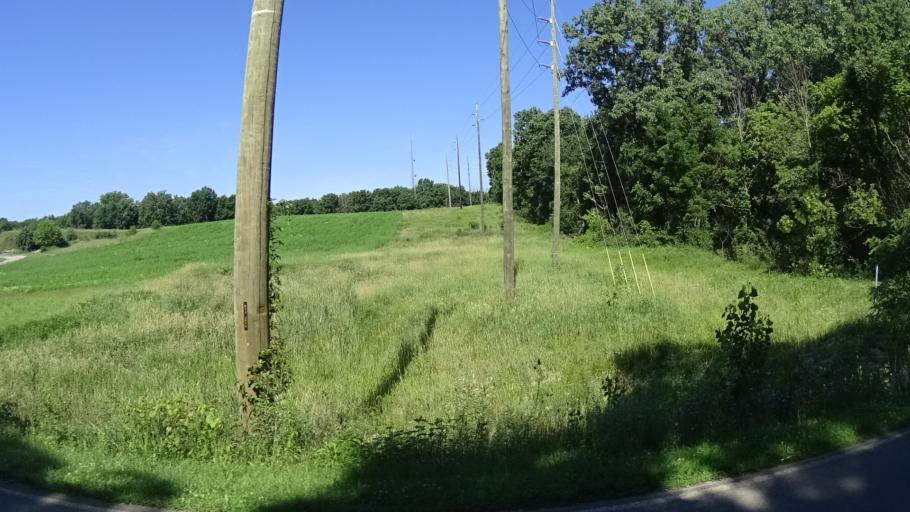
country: US
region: Indiana
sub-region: Madison County
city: Pendleton
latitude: 40.0004
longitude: -85.7565
